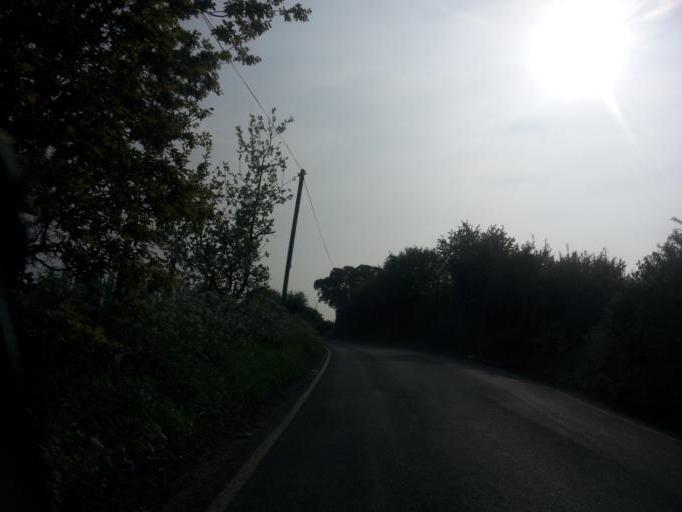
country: GB
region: England
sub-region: Kent
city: Newington
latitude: 51.3774
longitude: 0.6878
